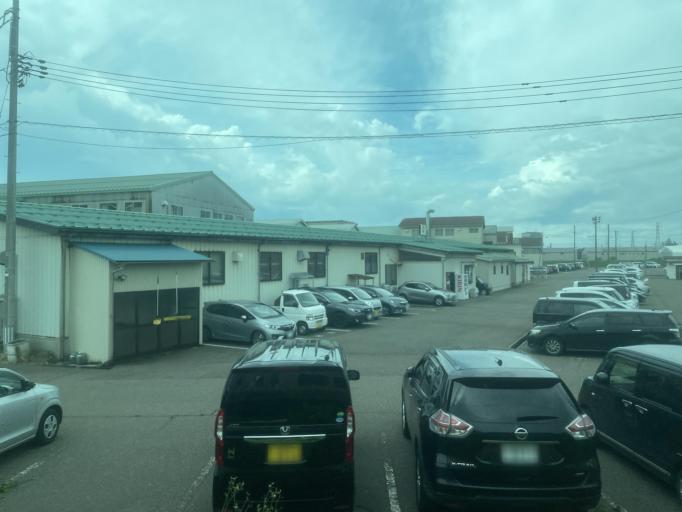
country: JP
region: Niigata
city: Joetsu
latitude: 37.1760
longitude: 138.2574
